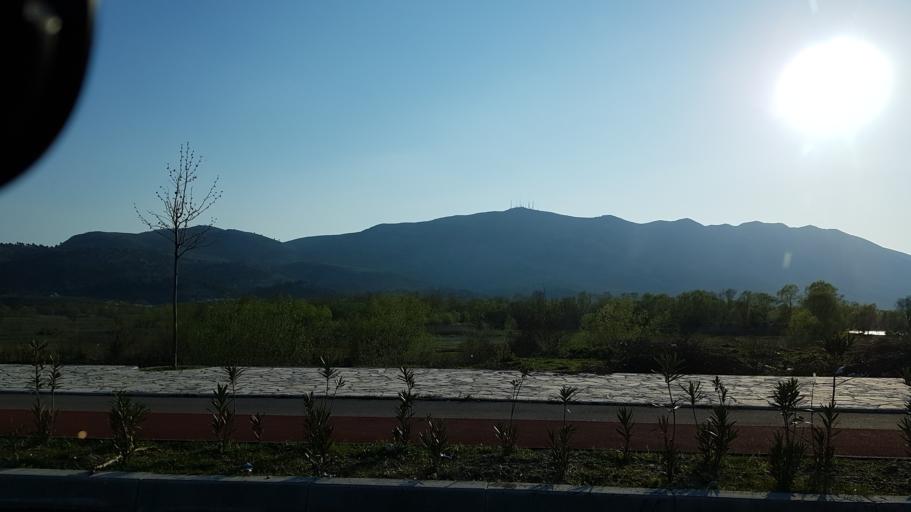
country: AL
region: Shkoder
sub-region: Rrethi i Shkodres
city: Shkoder
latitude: 42.0651
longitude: 19.4902
